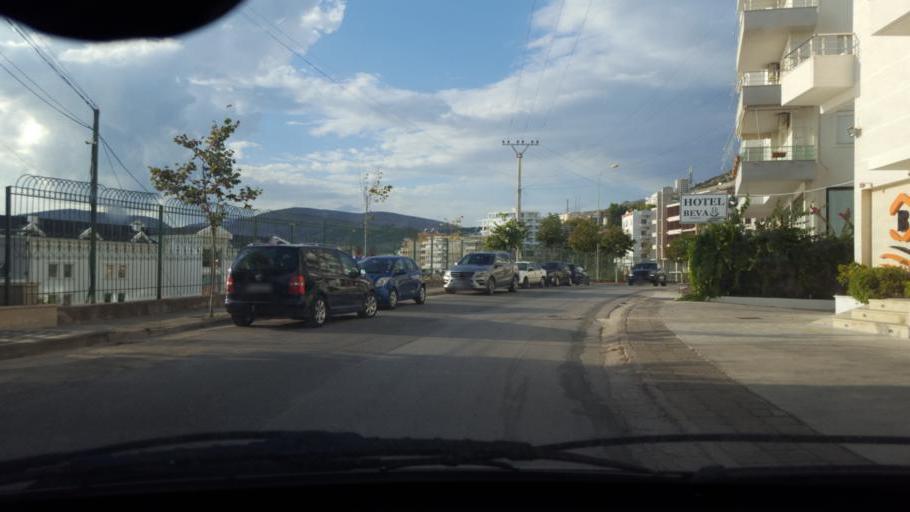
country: AL
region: Vlore
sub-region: Rrethi i Sarandes
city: Sarande
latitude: 39.8572
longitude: 20.0206
